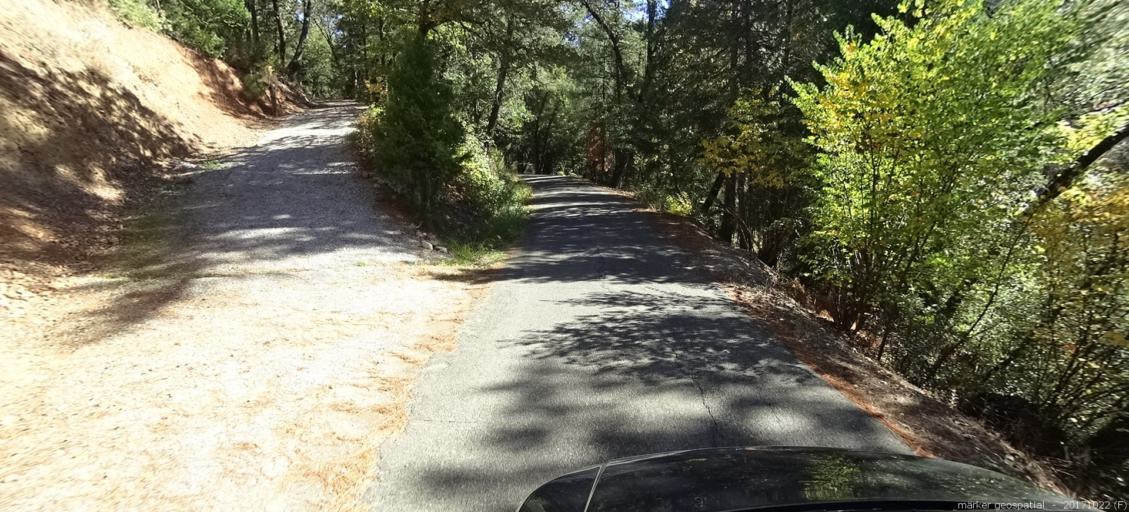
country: US
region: California
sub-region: Shasta County
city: Central Valley (historical)
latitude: 40.9326
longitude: -122.4679
